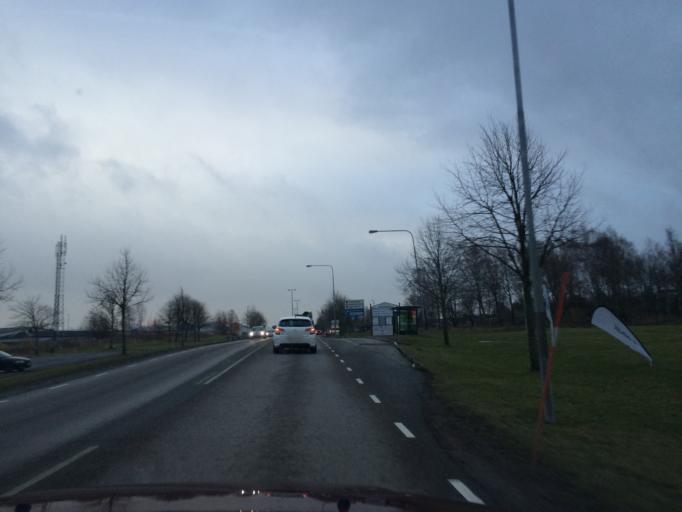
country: SE
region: Halland
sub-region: Kungsbacka Kommun
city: Kungsbacka
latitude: 57.5069
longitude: 12.0652
